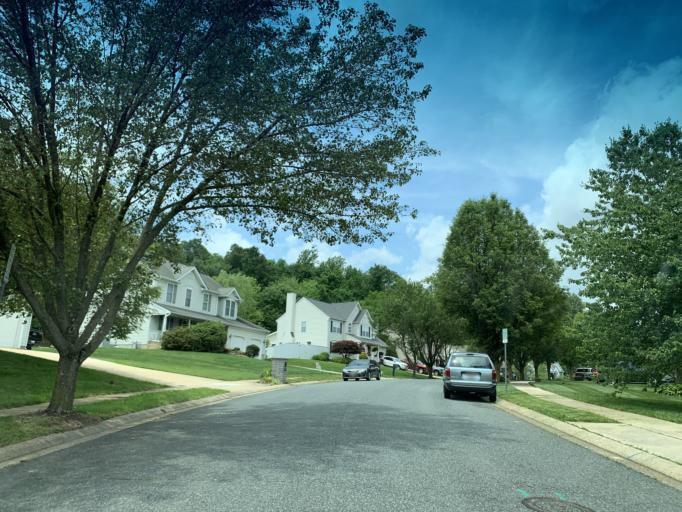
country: US
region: Maryland
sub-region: Harford County
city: South Bel Air
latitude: 39.5588
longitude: -76.3337
